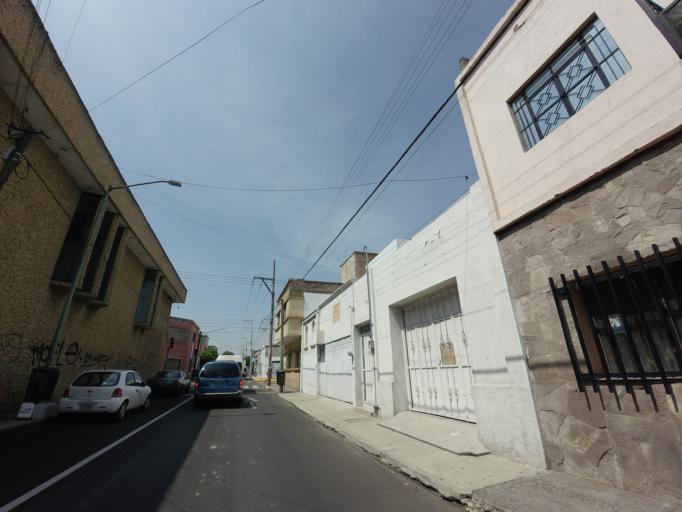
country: MX
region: Jalisco
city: Guadalajara
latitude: 20.6885
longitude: -103.3465
